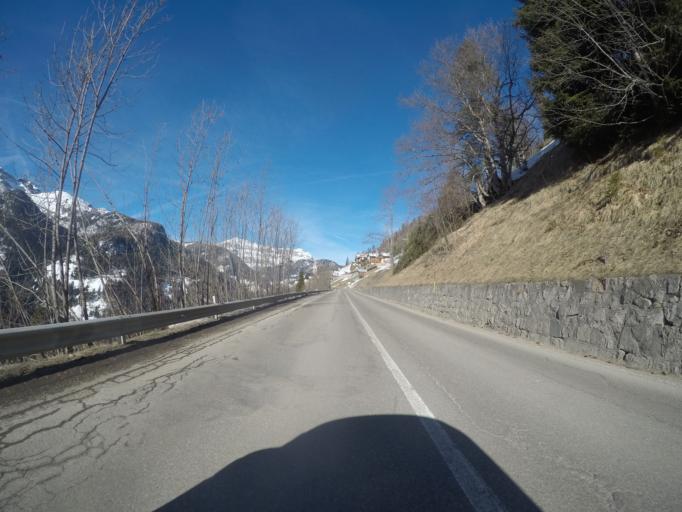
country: IT
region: Veneto
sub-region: Provincia di Belluno
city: Livinallongo del Col di Lana
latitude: 46.4785
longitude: 11.9605
